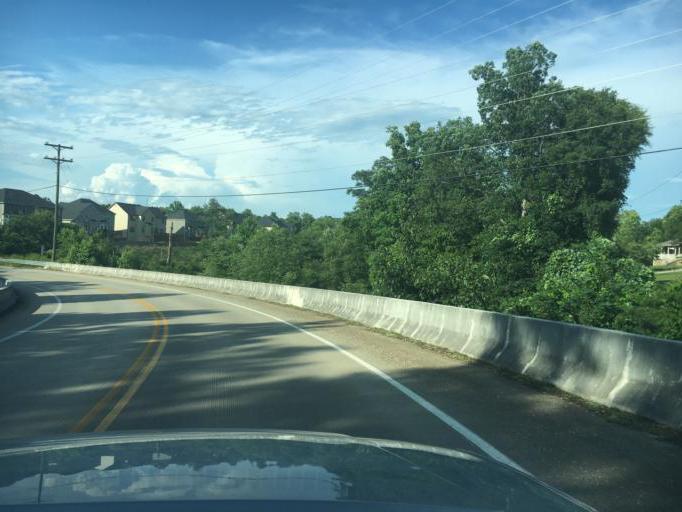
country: US
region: South Carolina
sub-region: Greenville County
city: Five Forks
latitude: 34.7932
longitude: -82.2310
